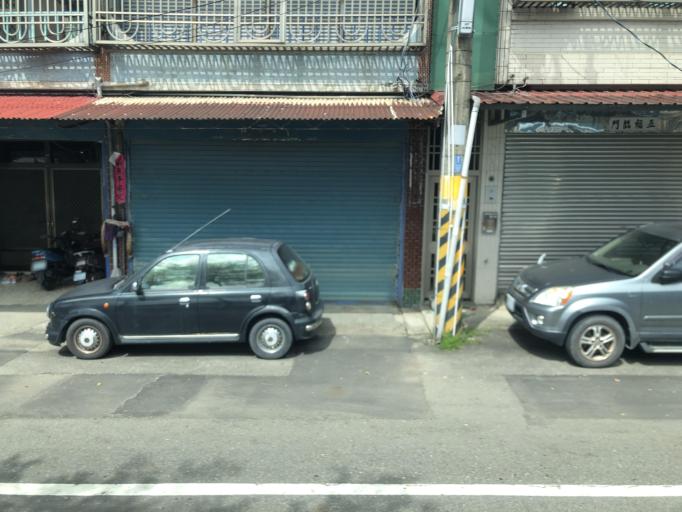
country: TW
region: Taiwan
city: Yujing
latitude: 22.9070
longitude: 120.5586
